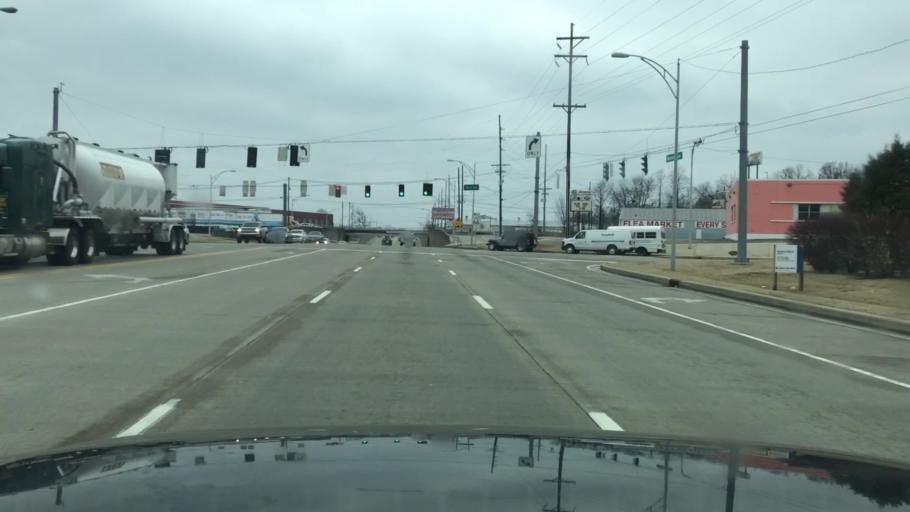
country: US
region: Indiana
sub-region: Vanderburgh County
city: Evansville
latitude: 37.9991
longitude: -87.5383
